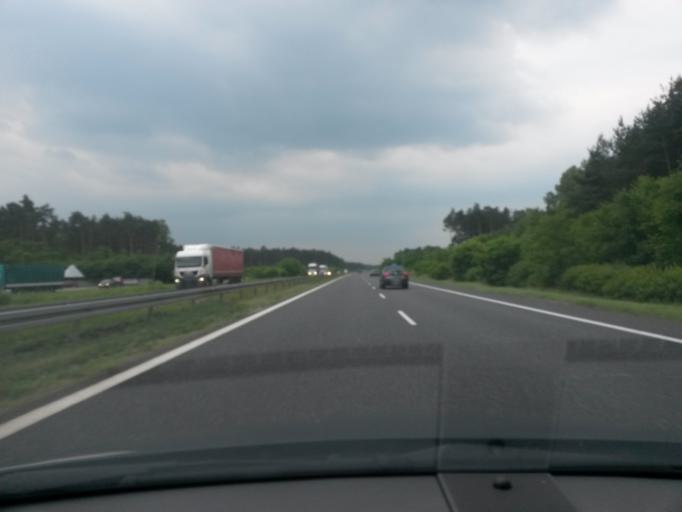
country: PL
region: Lodz Voivodeship
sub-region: Powiat radomszczanski
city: Radomsko
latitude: 51.0460
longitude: 19.3492
